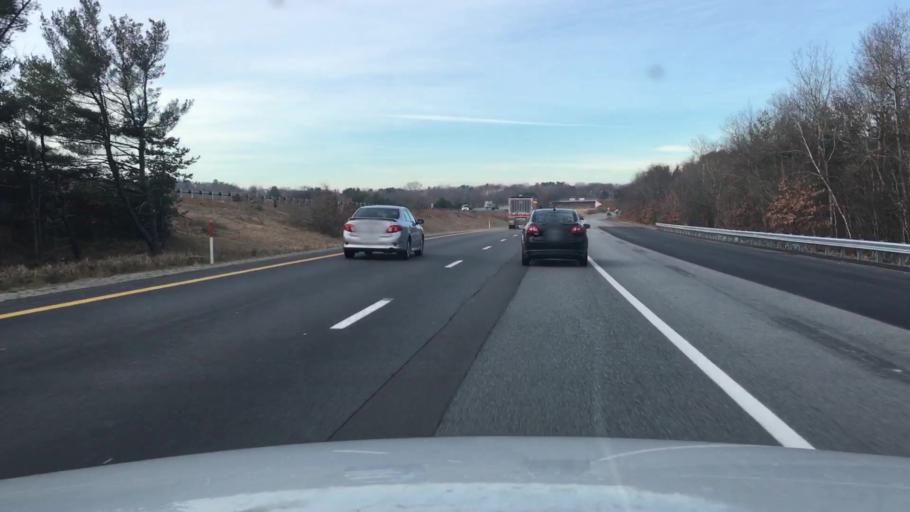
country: US
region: New Hampshire
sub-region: Hillsborough County
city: Manchester
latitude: 42.9621
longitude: -71.4096
